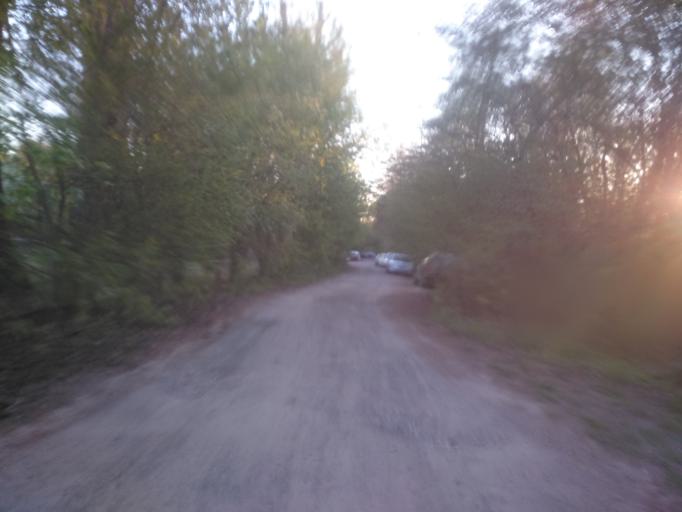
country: DE
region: Berlin
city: Stadtrandsiedlung Malchow
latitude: 52.5742
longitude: 13.4691
